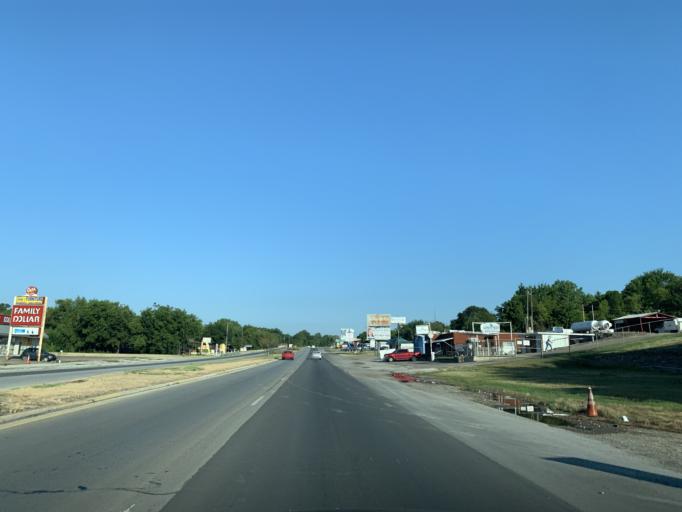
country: US
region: Texas
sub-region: Tarrant County
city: Sansom Park
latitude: 32.7962
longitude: -97.3987
